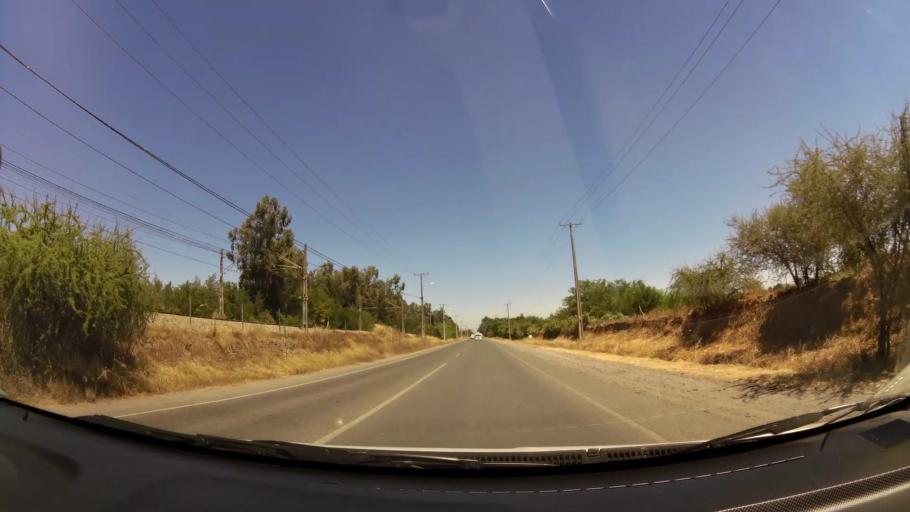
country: CL
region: O'Higgins
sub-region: Provincia de Cachapoal
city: Rancagua
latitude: -34.2325
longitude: -70.7876
